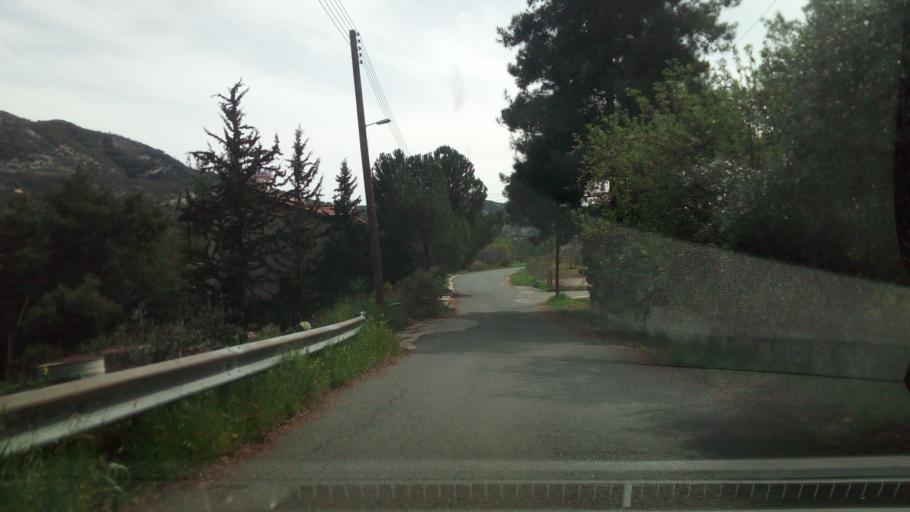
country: CY
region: Limassol
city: Pelendri
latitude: 34.8598
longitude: 32.9102
